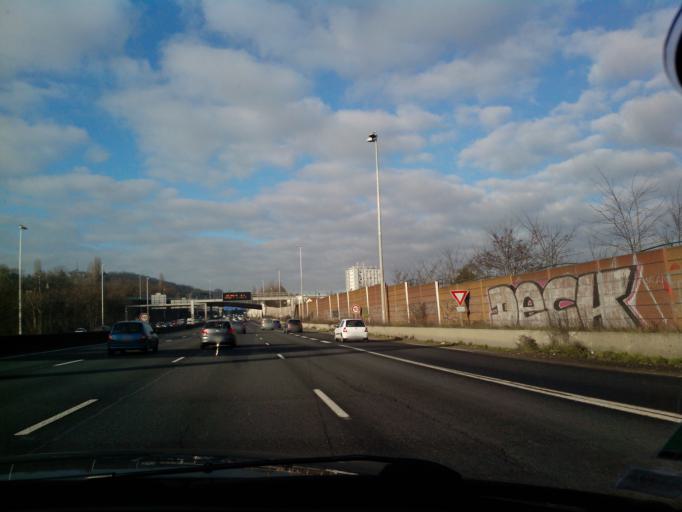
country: FR
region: Ile-de-France
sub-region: Departement du Val-d'Oise
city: Sannois
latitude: 48.9653
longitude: 2.2600
